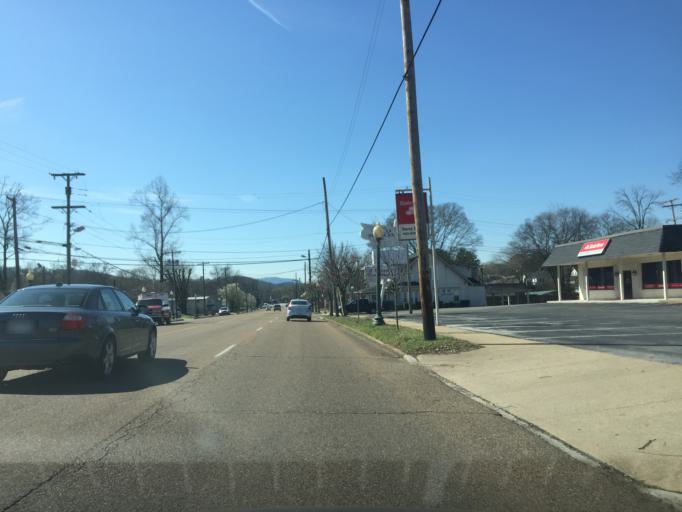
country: US
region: Tennessee
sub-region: Hamilton County
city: Red Bank
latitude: 35.1130
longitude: -85.2936
